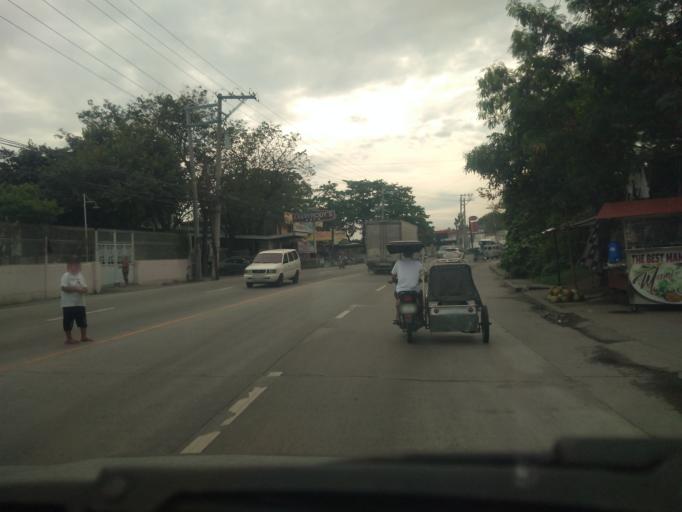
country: PH
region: Central Luzon
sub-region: Province of Pampanga
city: Del Pilar
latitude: 15.0326
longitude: 120.6956
